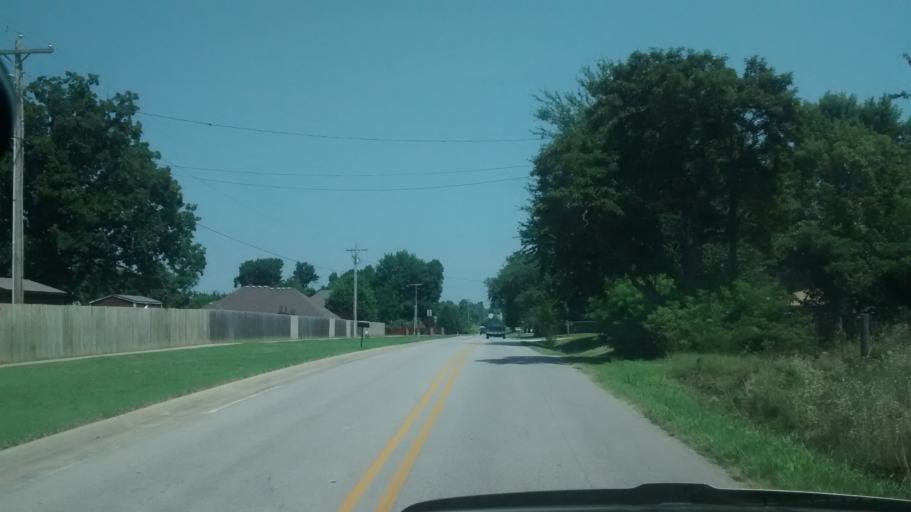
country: US
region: Arkansas
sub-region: Washington County
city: Farmington
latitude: 36.0689
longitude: -94.2534
